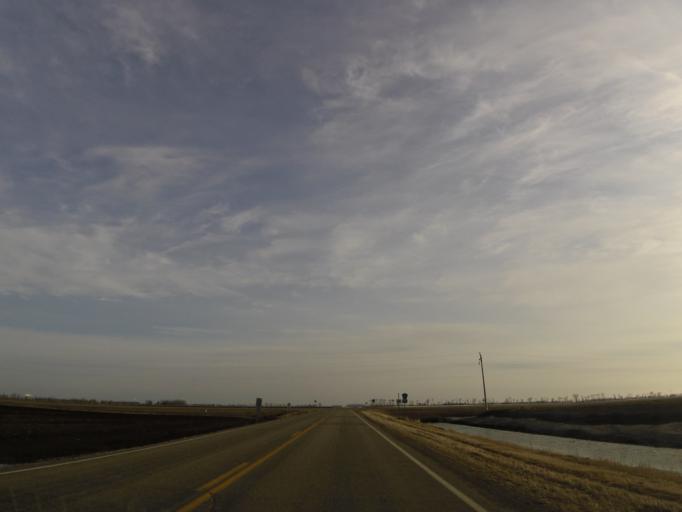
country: US
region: North Dakota
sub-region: Walsh County
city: Grafton
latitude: 48.4137
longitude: -97.2996
